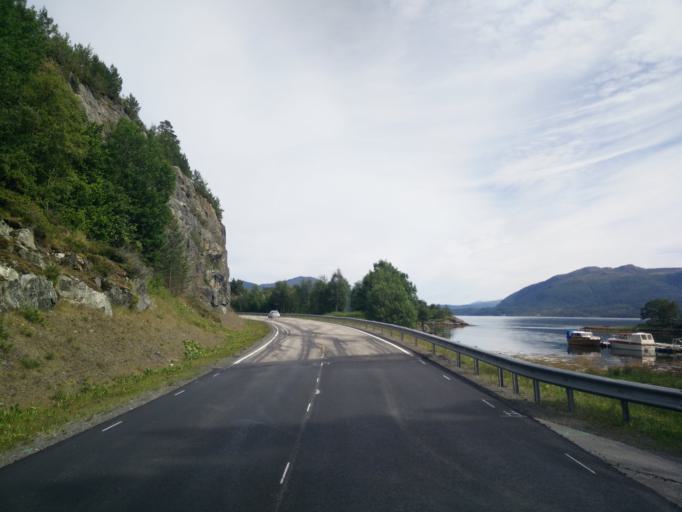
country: NO
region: More og Romsdal
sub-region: Kristiansund
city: Rensvik
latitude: 62.9921
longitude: 7.9034
